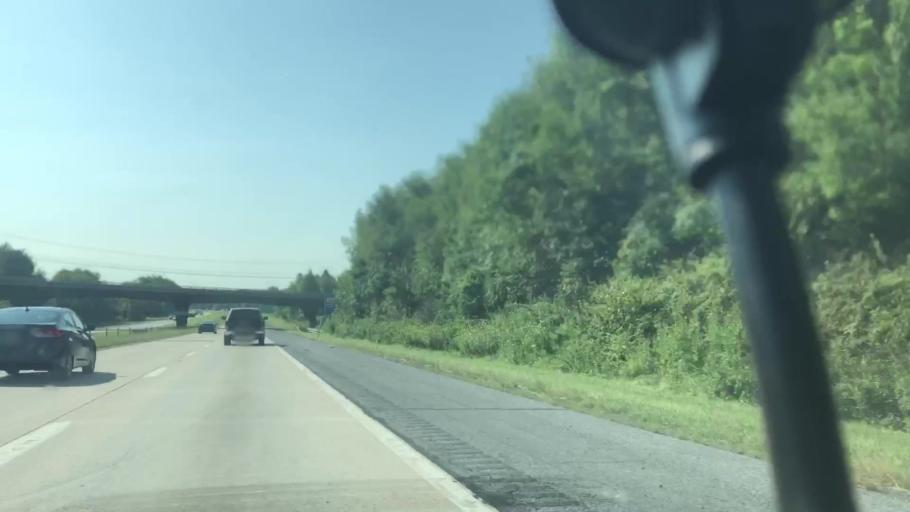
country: US
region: Pennsylvania
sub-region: Montgomery County
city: Royersford
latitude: 40.2048
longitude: -75.5363
